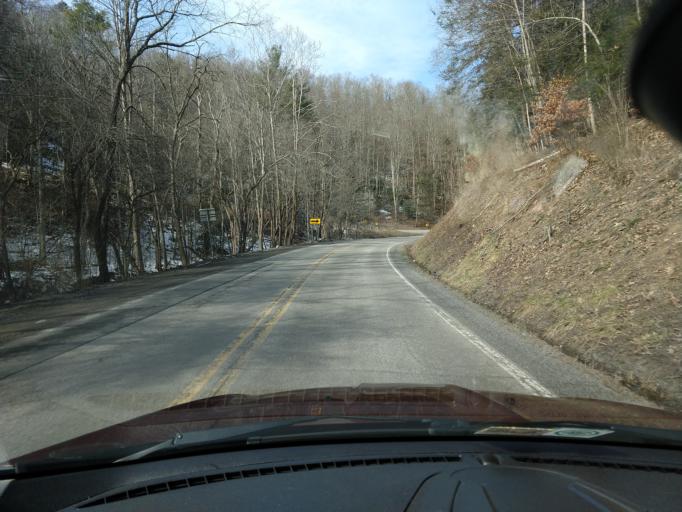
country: US
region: West Virginia
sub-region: Pocahontas County
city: Marlinton
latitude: 38.1851
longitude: -80.1365
